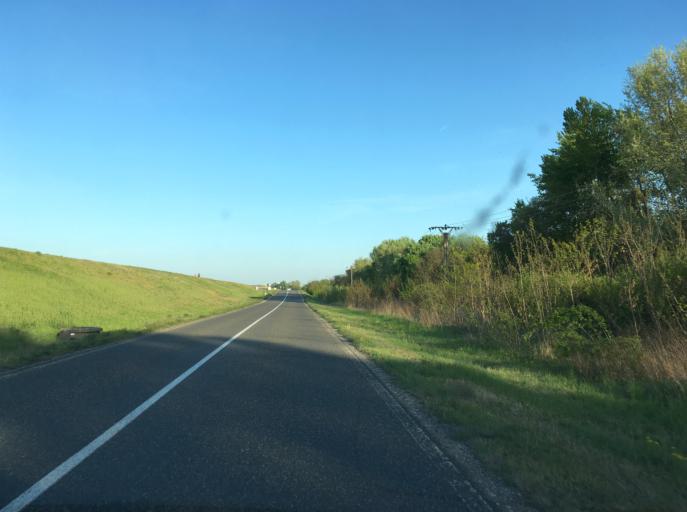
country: SK
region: Trnavsky
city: Samorin
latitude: 48.0020
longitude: 17.2583
